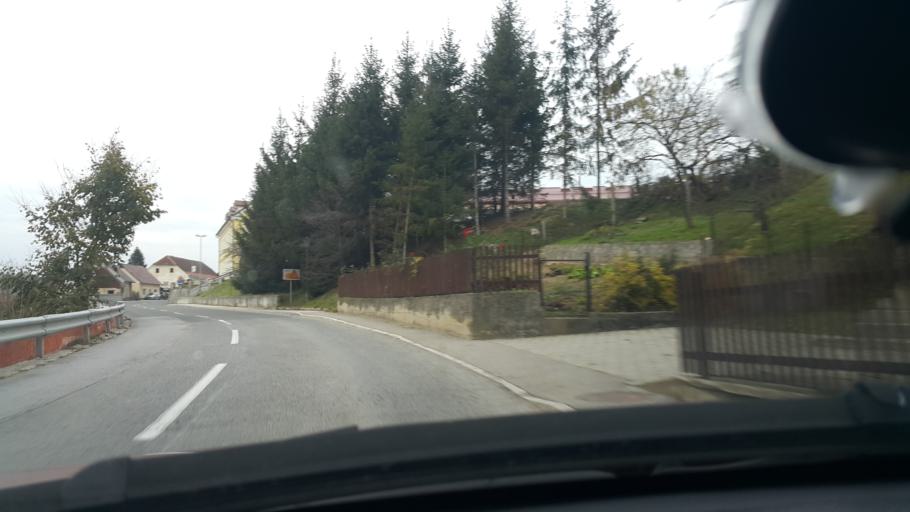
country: SI
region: Bistrica ob Sotli
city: Bistrica ob Sotli
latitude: 46.0547
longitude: 15.6644
